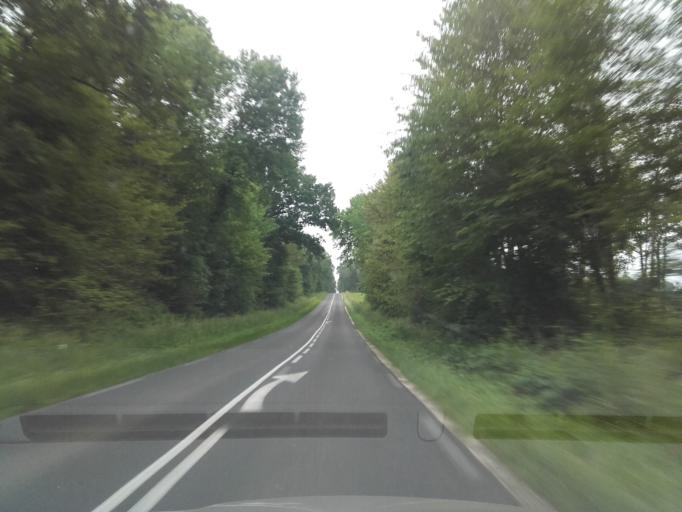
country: FR
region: Centre
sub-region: Departement d'Indre-et-Loire
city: Beaumont-la-Ronce
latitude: 47.5928
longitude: 0.6646
